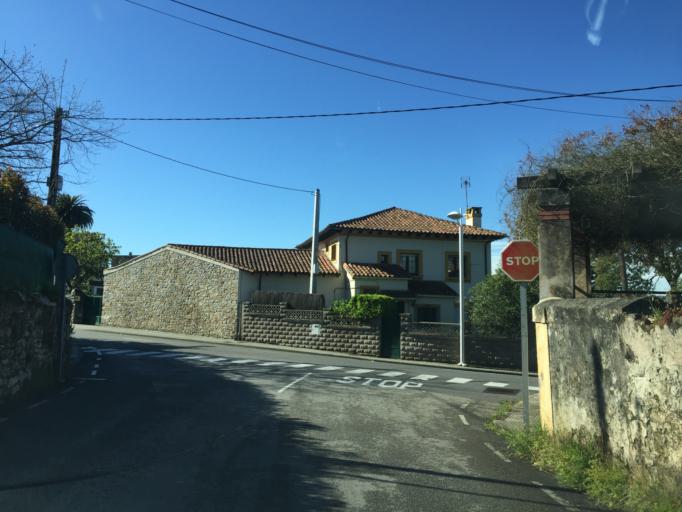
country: ES
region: Asturias
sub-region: Province of Asturias
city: Gijon
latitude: 43.5379
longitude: -5.6226
